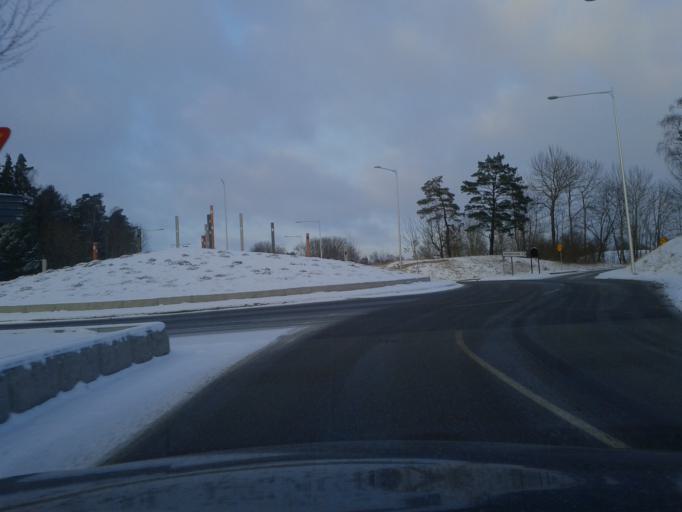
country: SE
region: Stockholm
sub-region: Taby Kommun
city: Taby
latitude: 59.4530
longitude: 18.0867
